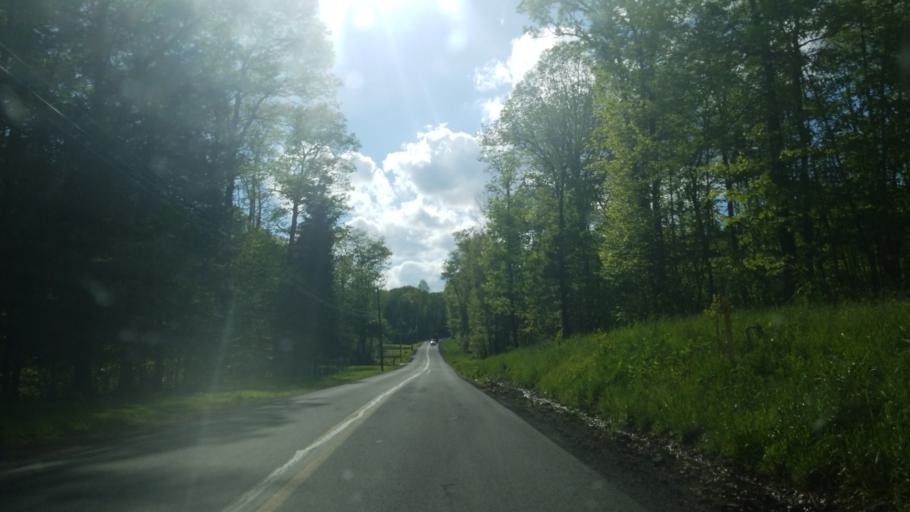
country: US
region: Pennsylvania
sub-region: Clearfield County
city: Osceola Mills
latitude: 40.9340
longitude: -78.3075
